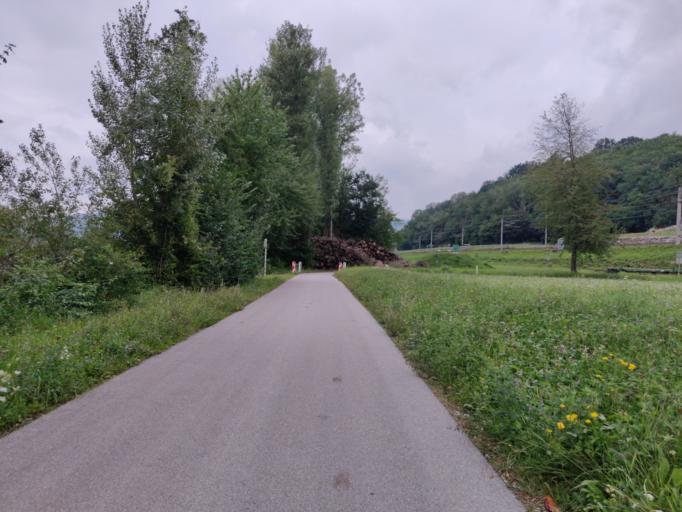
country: AT
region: Lower Austria
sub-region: Politischer Bezirk Melk
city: Ybbs an der Donau
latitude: 48.1832
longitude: 15.1197
